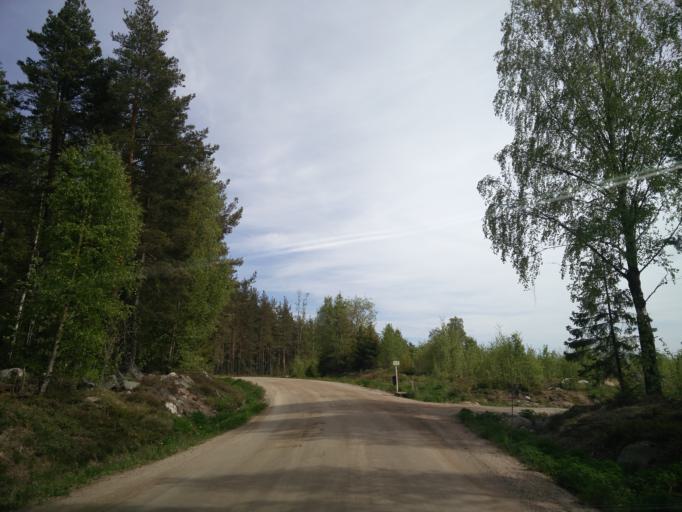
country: SE
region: Gaevleborg
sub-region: Hudiksvalls Kommun
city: Sorforsa
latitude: 61.7382
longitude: 16.9523
